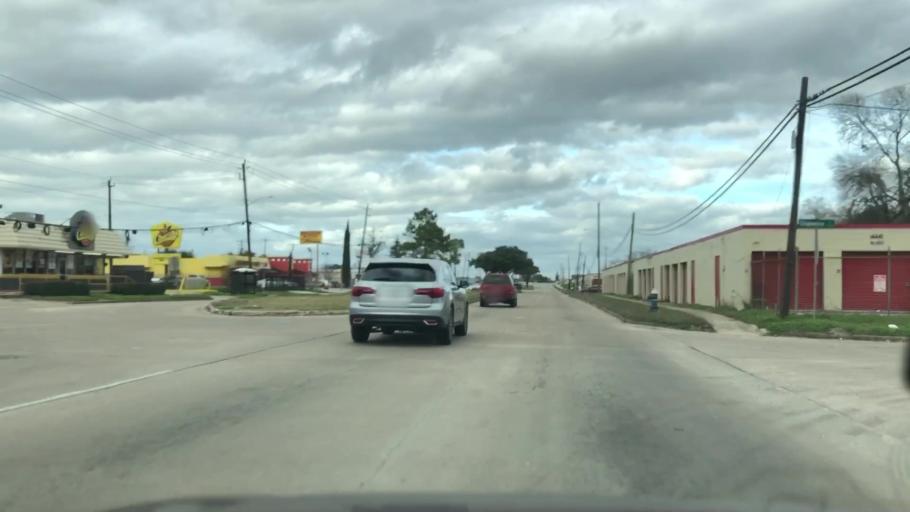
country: US
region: Texas
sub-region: Fort Bend County
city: Missouri City
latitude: 29.6162
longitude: -95.4649
